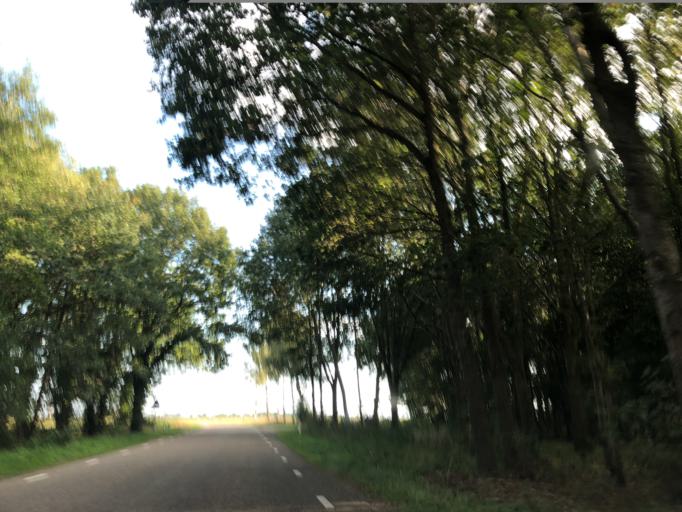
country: NL
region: Groningen
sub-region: Gemeente Vlagtwedde
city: Sellingen
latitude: 53.0050
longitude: 7.1848
